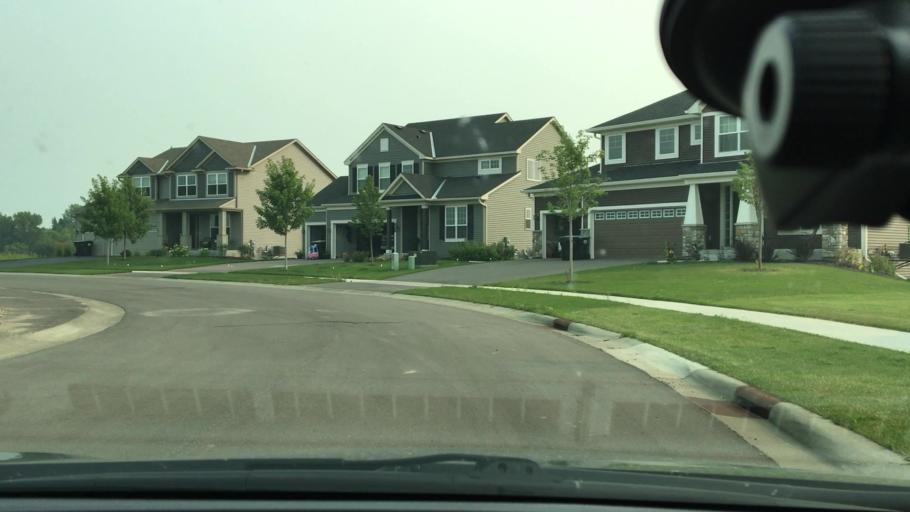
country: US
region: Minnesota
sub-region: Wright County
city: Otsego
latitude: 45.2615
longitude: -93.5690
